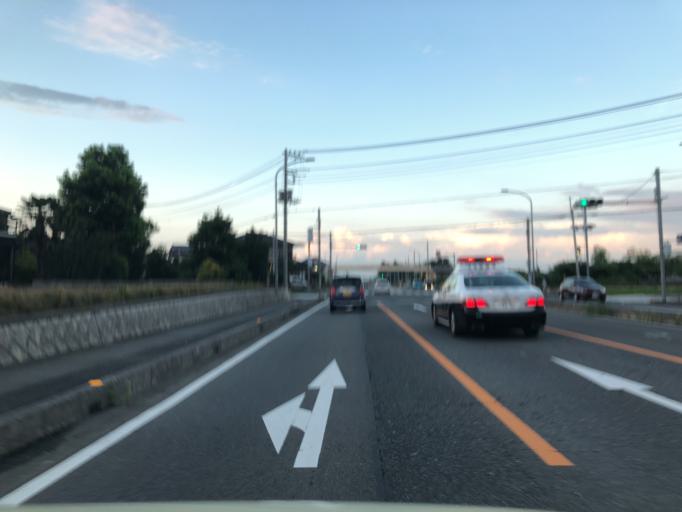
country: JP
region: Saitama
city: Sakado
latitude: 36.0185
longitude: 139.4105
